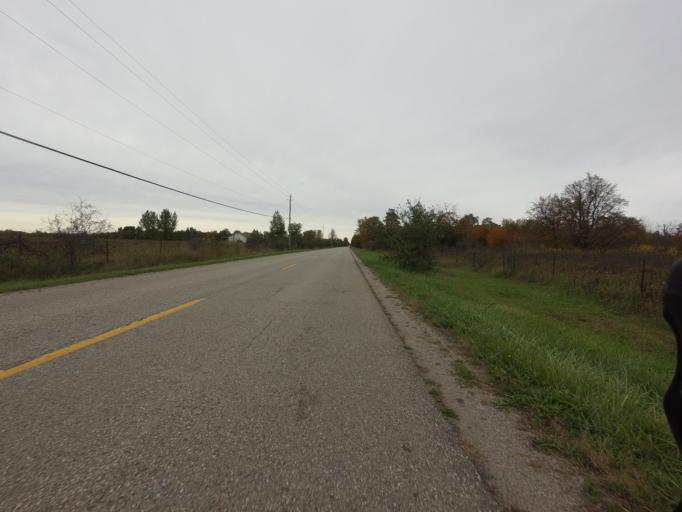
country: CA
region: Ontario
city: Brockville
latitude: 44.6830
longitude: -75.8534
